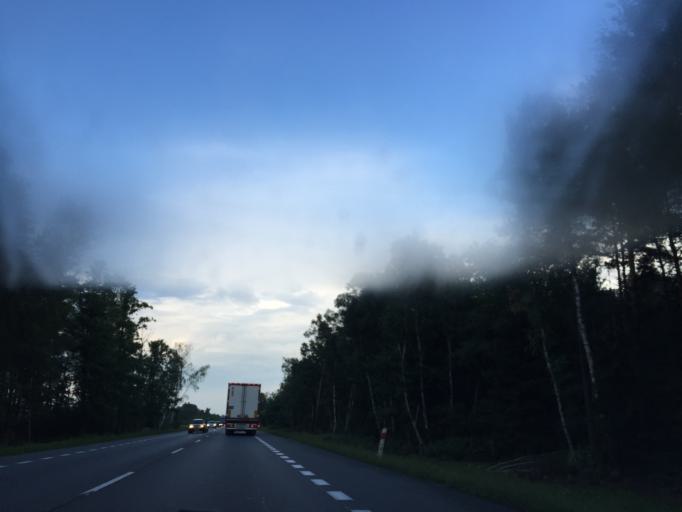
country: PL
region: Masovian Voivodeship
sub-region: Powiat minski
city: Minsk Mazowiecki
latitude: 52.1596
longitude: 21.5171
